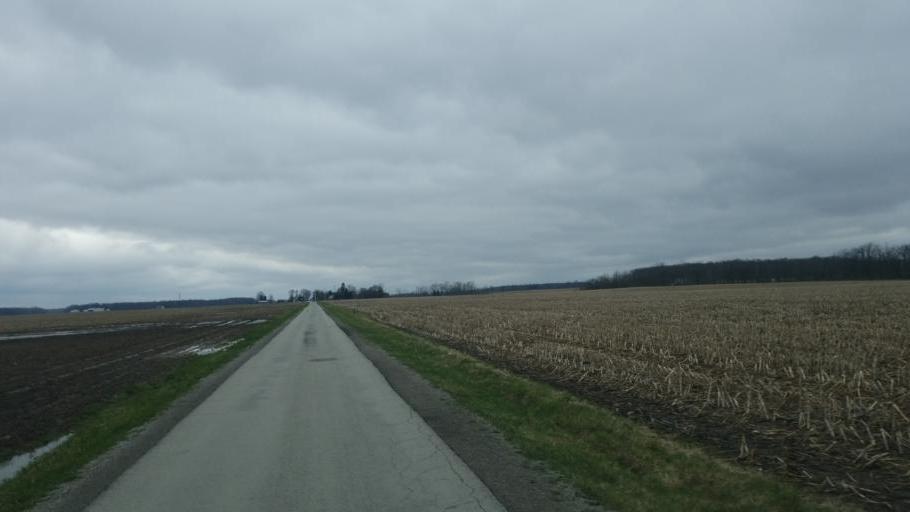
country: US
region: Ohio
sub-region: Hardin County
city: Forest
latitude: 40.7234
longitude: -83.4894
